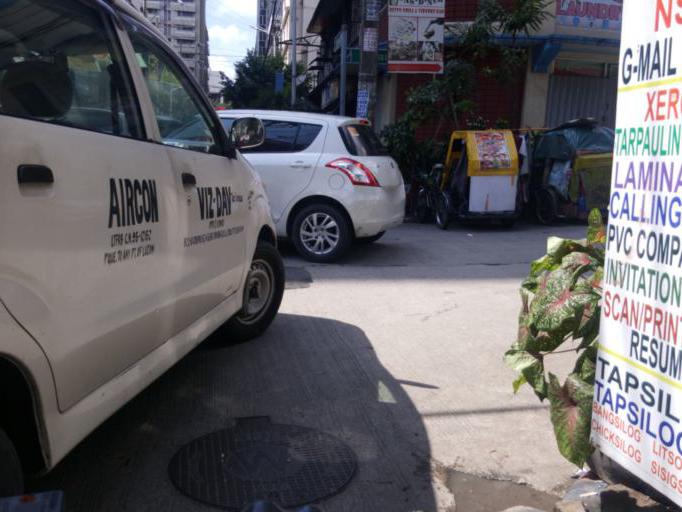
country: PH
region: Metro Manila
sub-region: City of Manila
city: Port Area
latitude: 14.5790
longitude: 120.9805
